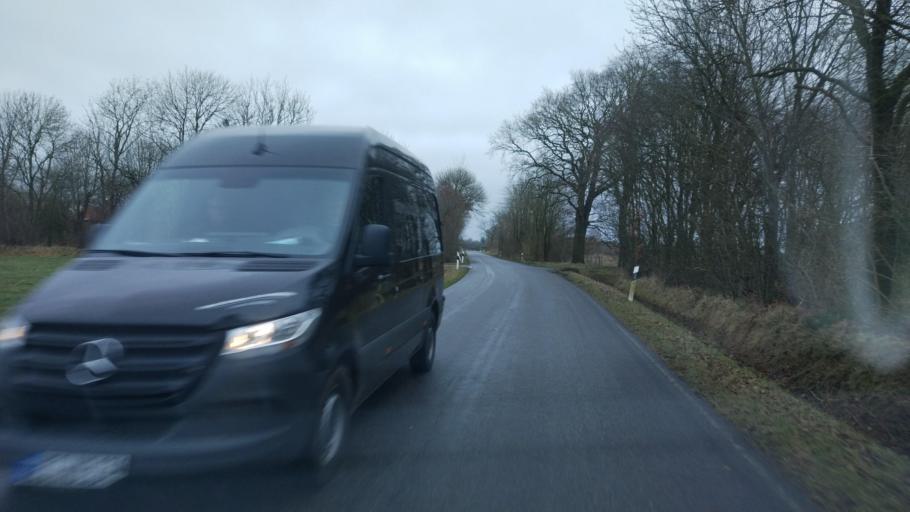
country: DE
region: Schleswig-Holstein
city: Ellingstedt
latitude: 54.4828
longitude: 9.3701
